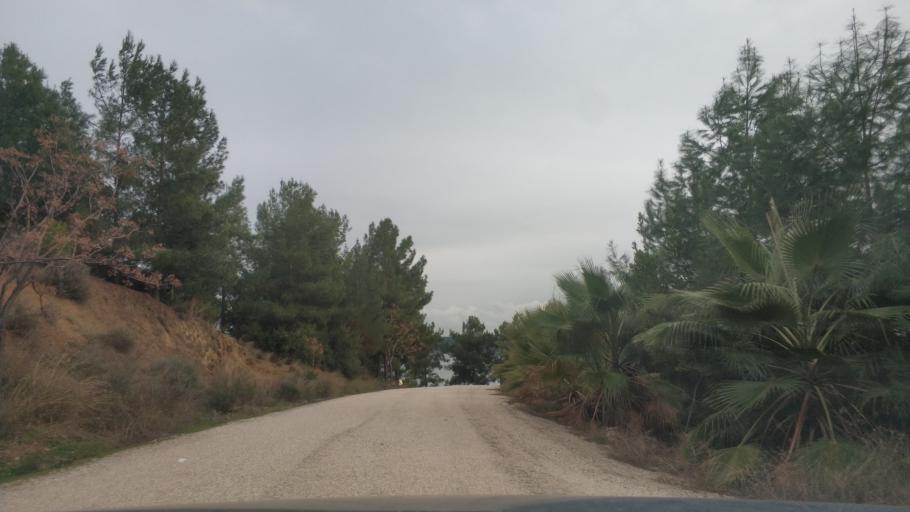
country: TR
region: Adana
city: Adana
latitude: 37.0785
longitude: 35.3269
